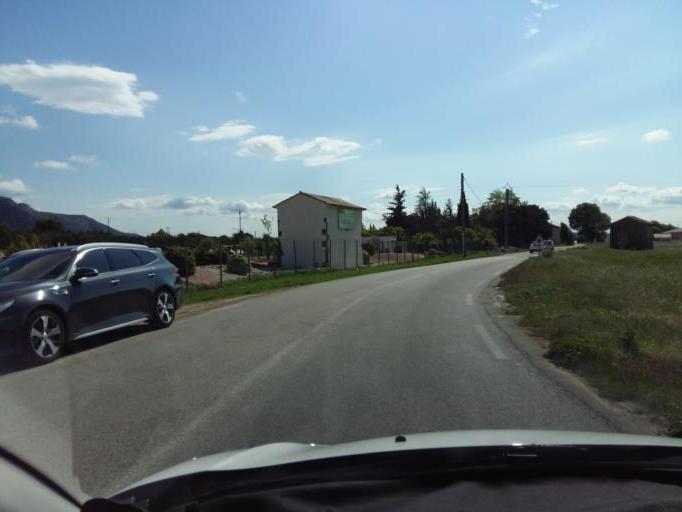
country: FR
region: Provence-Alpes-Cote d'Azur
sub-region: Departement du Vaucluse
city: Robion
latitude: 43.8687
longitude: 5.1247
